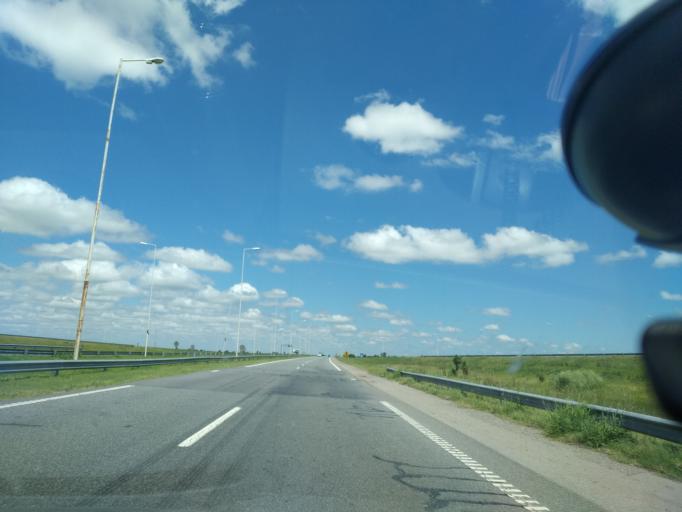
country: AR
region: Cordoba
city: Oliva
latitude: -32.0196
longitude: -63.5351
